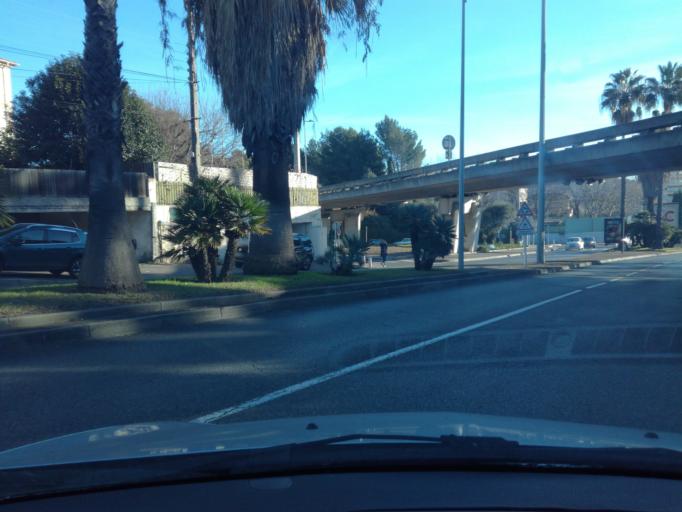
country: FR
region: Provence-Alpes-Cote d'Azur
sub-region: Departement des Alpes-Maritimes
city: Antibes
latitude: 43.5808
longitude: 7.1164
